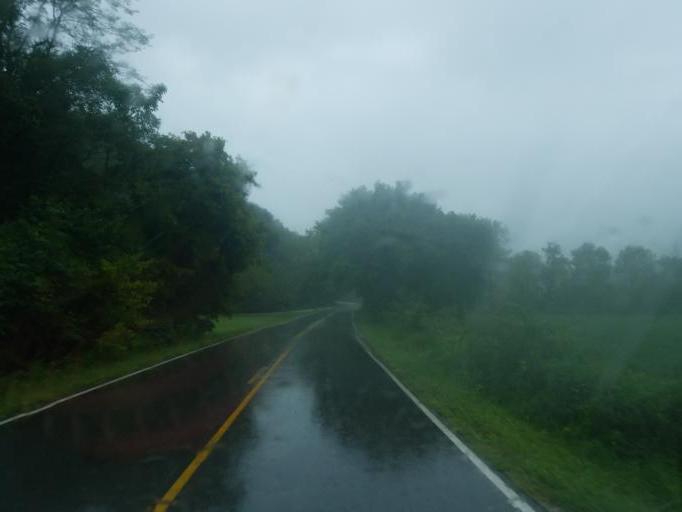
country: US
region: Kentucky
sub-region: Carter County
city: Grayson
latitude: 38.4949
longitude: -83.0114
